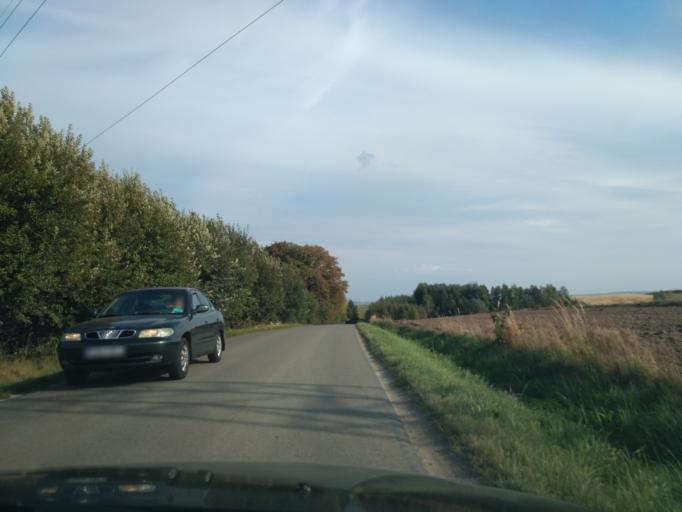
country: PL
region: Subcarpathian Voivodeship
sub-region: Powiat rzeszowski
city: Zglobien
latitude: 50.0055
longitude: 21.8646
